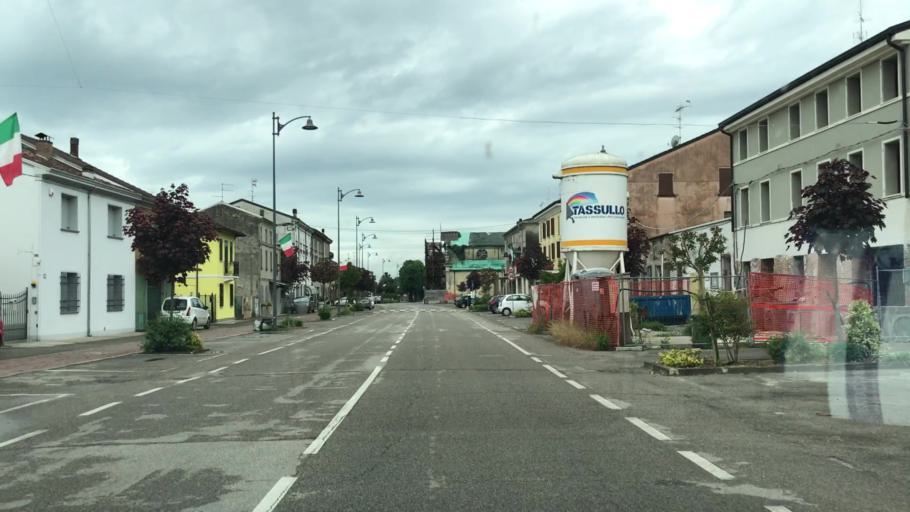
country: IT
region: Lombardy
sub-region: Provincia di Mantova
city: San Giovanni del Dosso
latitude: 44.9667
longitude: 11.0805
